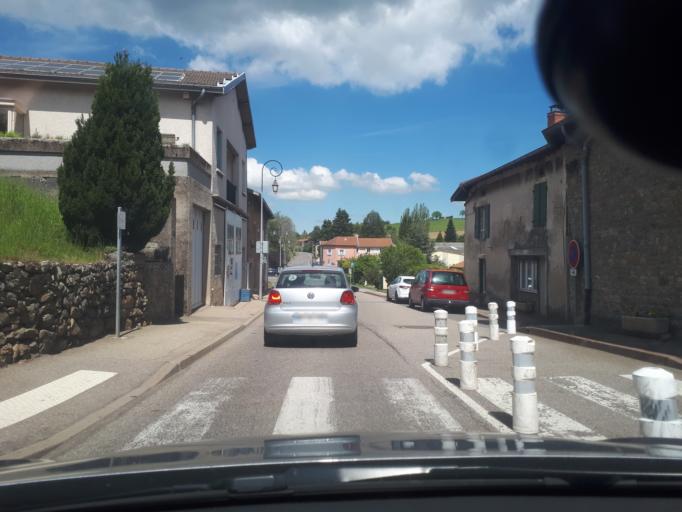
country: FR
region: Rhone-Alpes
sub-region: Departement du Rhone
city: Saint-Martin-en-Haut
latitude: 45.6846
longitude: 4.5290
